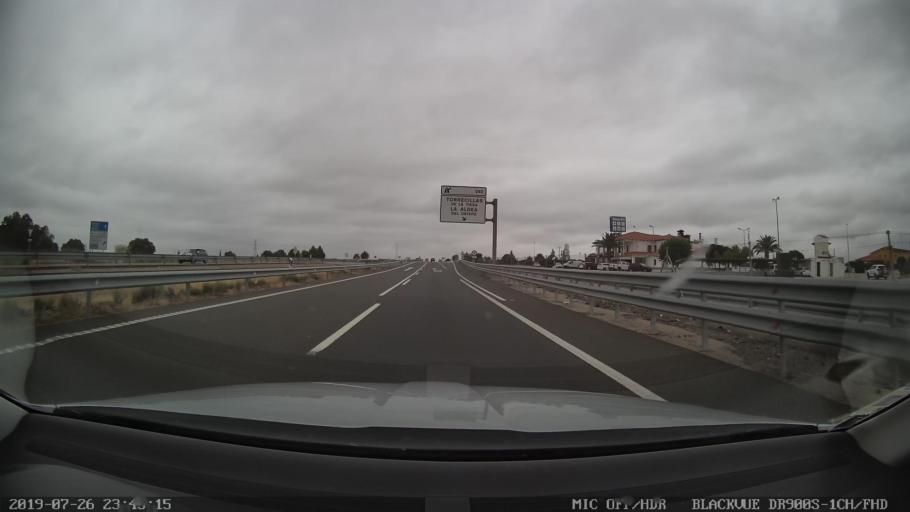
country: ES
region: Extremadura
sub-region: Provincia de Caceres
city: Torrecillas de la Tiesa
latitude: 39.5649
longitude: -5.8335
